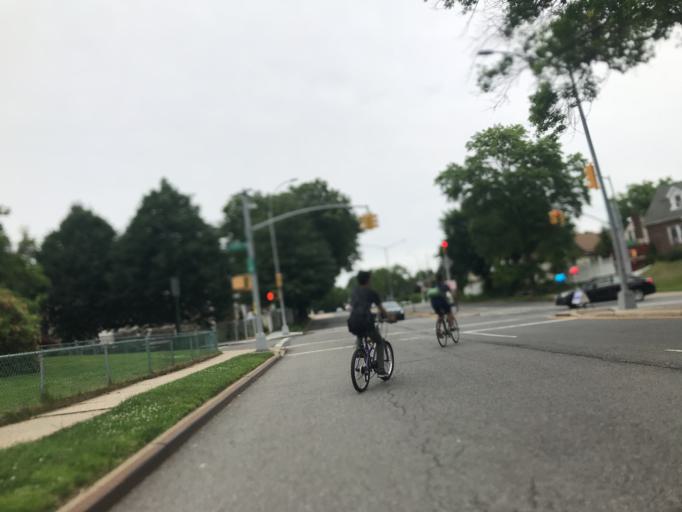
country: US
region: New York
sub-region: Queens County
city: Jamaica
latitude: 40.7465
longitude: -73.7925
